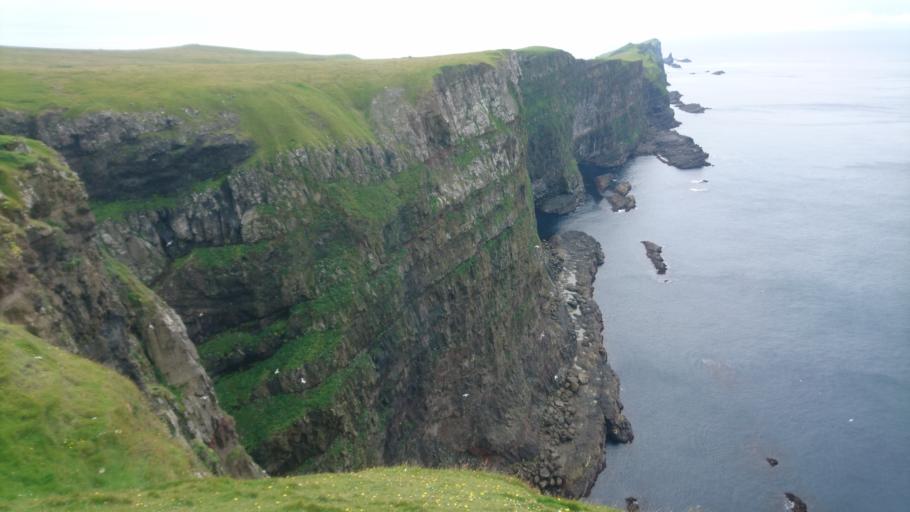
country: FO
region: Vagar
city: Sorvagur
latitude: 62.1121
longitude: -7.6247
